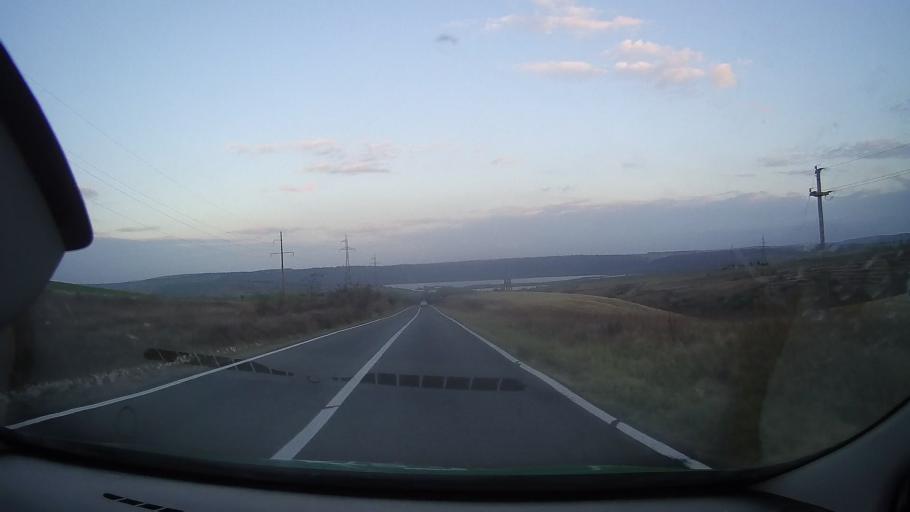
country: RO
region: Constanta
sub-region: Comuna Lipnita
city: Lipnita
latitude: 44.0968
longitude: 27.6171
